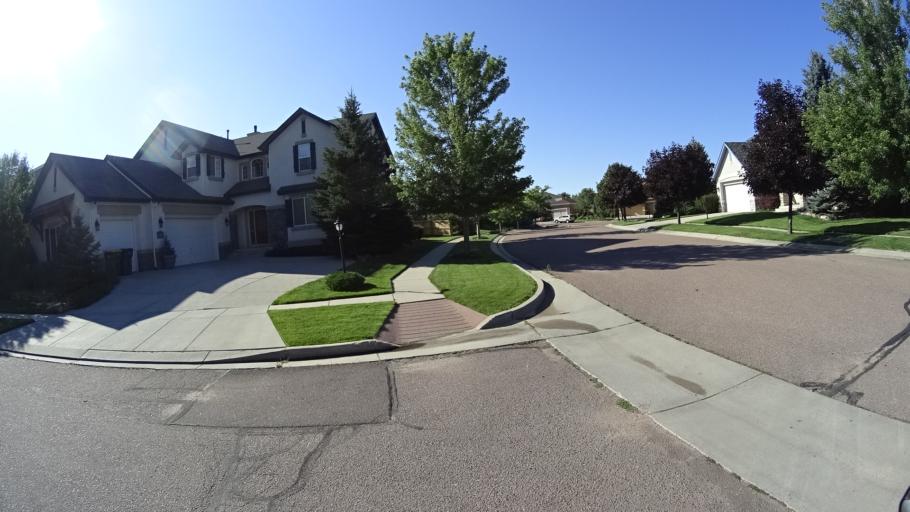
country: US
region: Colorado
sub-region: El Paso County
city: Black Forest
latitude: 38.9825
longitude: -104.7672
